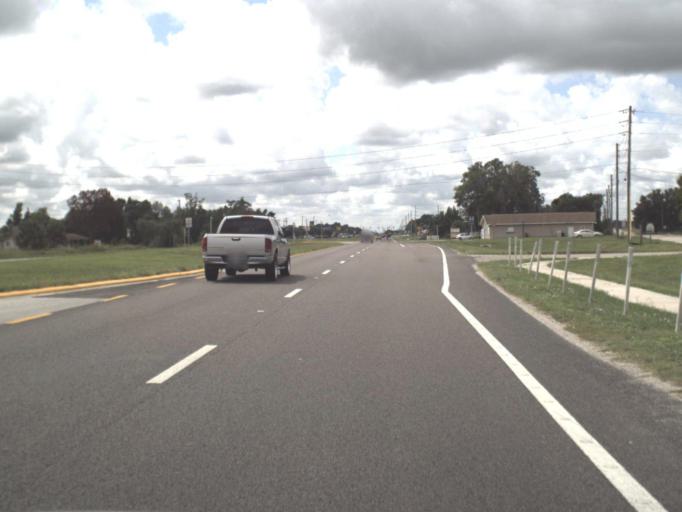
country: US
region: Florida
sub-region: Hardee County
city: Wauchula
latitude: 27.5751
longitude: -81.8175
